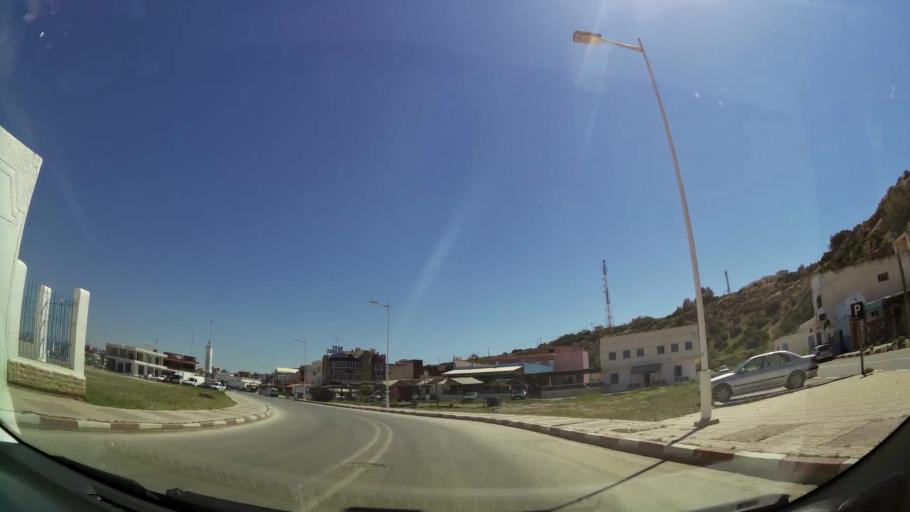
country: MA
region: Oriental
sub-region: Berkane-Taourirt
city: Madagh
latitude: 35.1435
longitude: -2.4241
